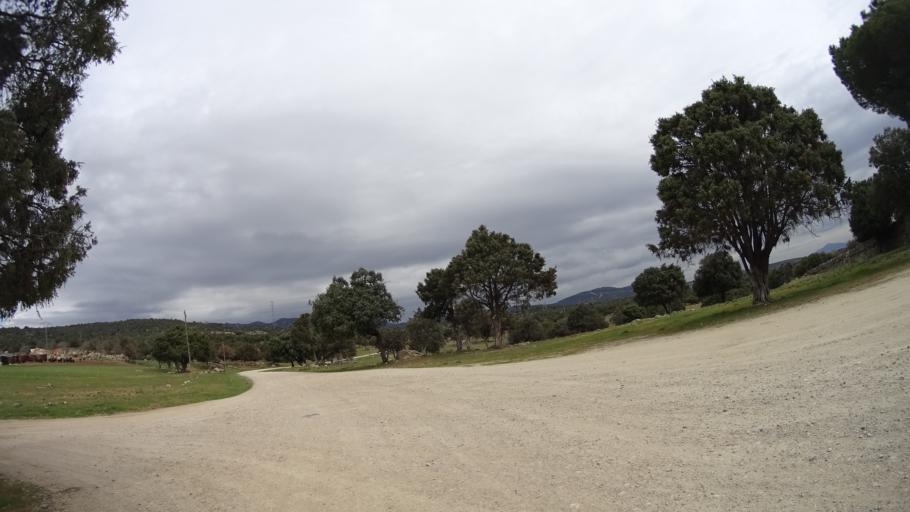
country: ES
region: Madrid
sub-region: Provincia de Madrid
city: Hoyo de Manzanares
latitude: 40.6067
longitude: -3.8766
